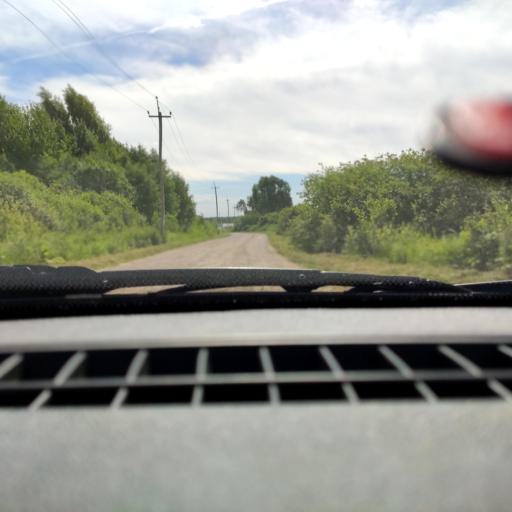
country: RU
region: Bashkortostan
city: Kabakovo
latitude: 54.7285
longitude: 56.2035
